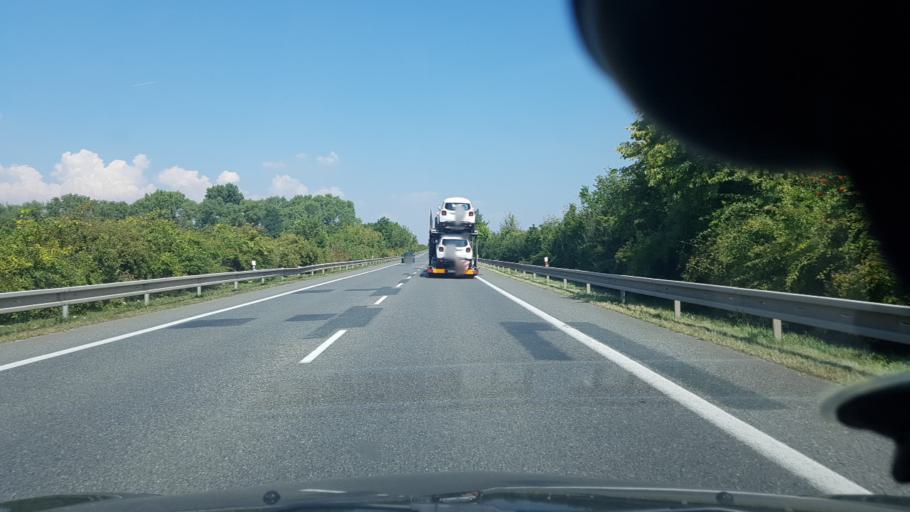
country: CZ
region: South Moravian
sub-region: Okres Breclav
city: Dolni Dunajovice
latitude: 48.8388
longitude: 16.6118
